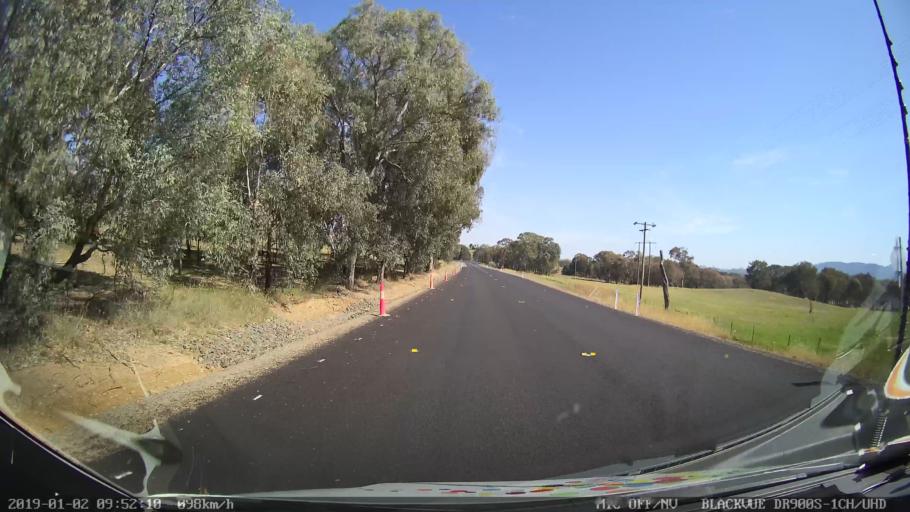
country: AU
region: New South Wales
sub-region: Tumut Shire
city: Tumut
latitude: -35.2642
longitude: 148.2086
